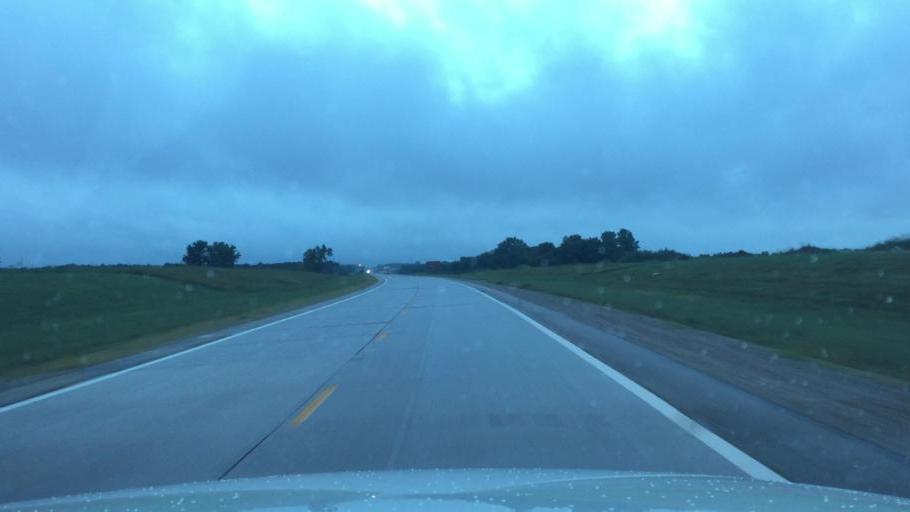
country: US
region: Kansas
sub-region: Neosho County
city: Chanute
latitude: 37.7152
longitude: -95.4789
